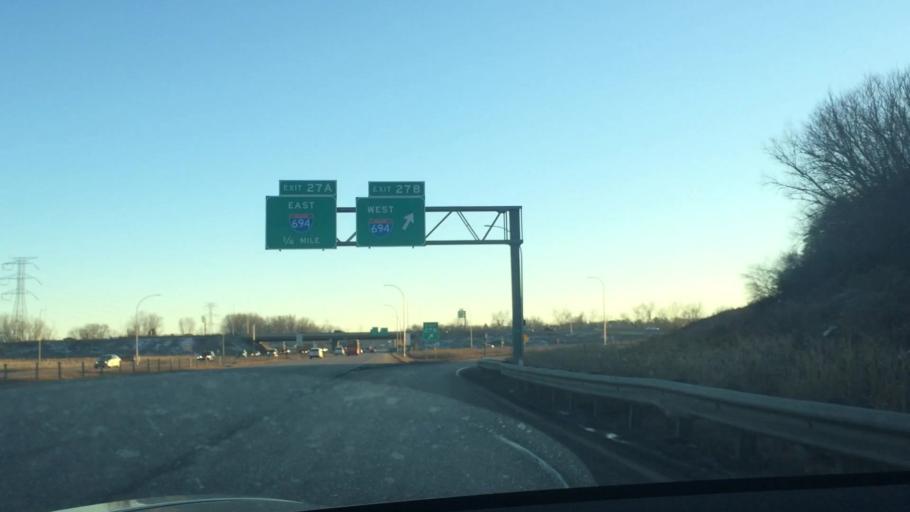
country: US
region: Minnesota
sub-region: Ramsey County
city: New Brighton
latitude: 45.0701
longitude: -93.1860
